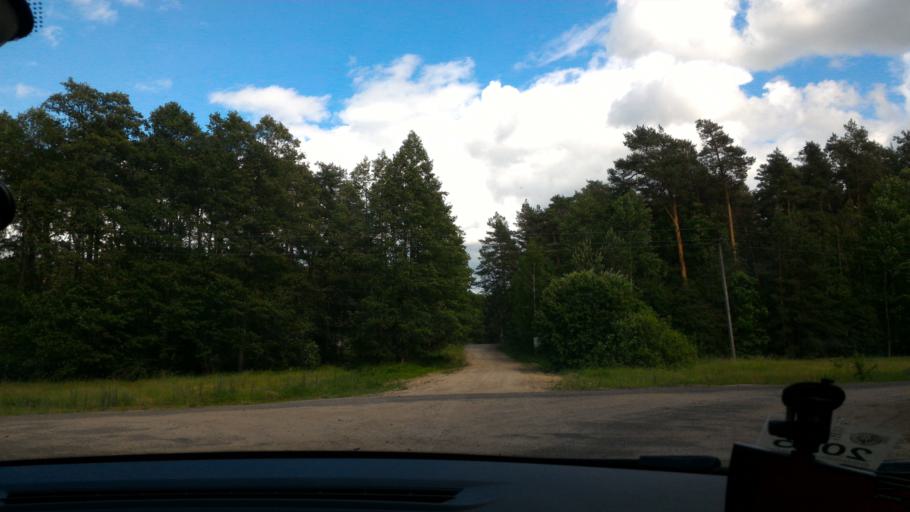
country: BY
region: Brest
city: Tsyelyakhany
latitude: 52.7841
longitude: 25.6592
